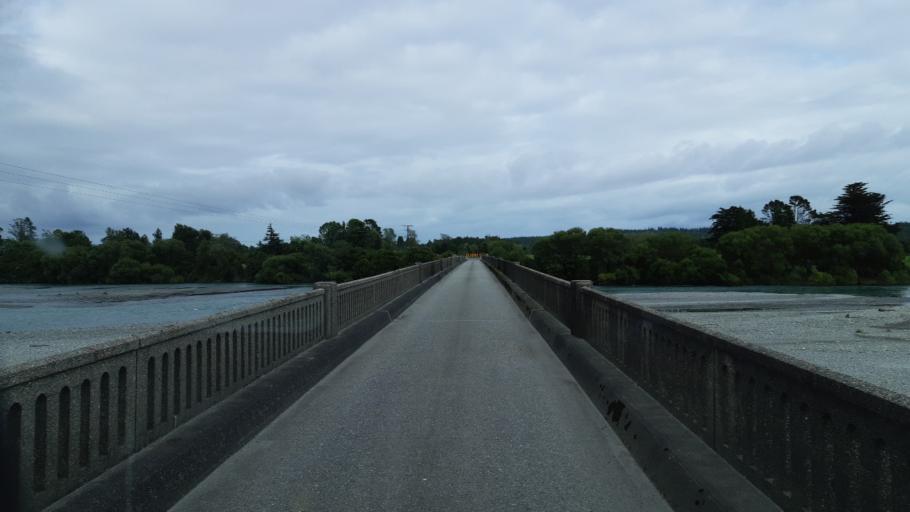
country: NZ
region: West Coast
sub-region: Westland District
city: Hokitika
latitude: -42.8357
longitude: 171.0215
